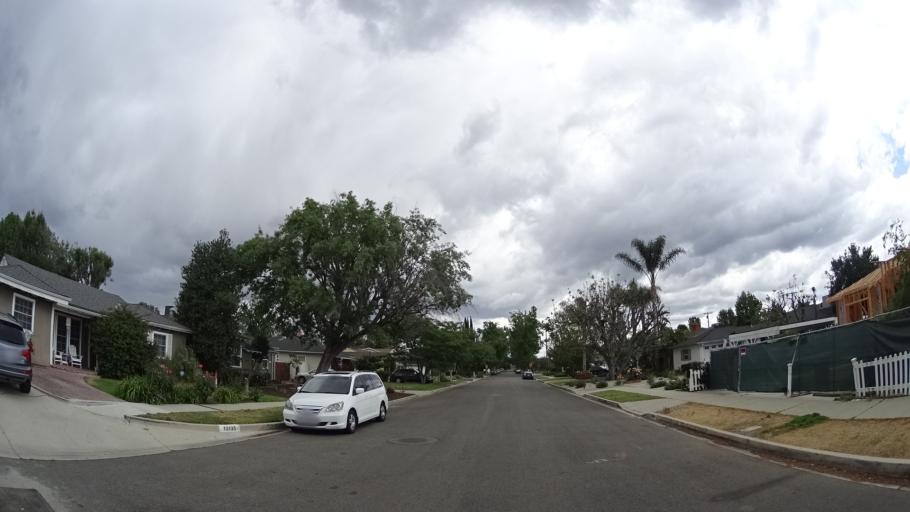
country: US
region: California
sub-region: Los Angeles County
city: Sherman Oaks
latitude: 34.1630
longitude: -118.4195
